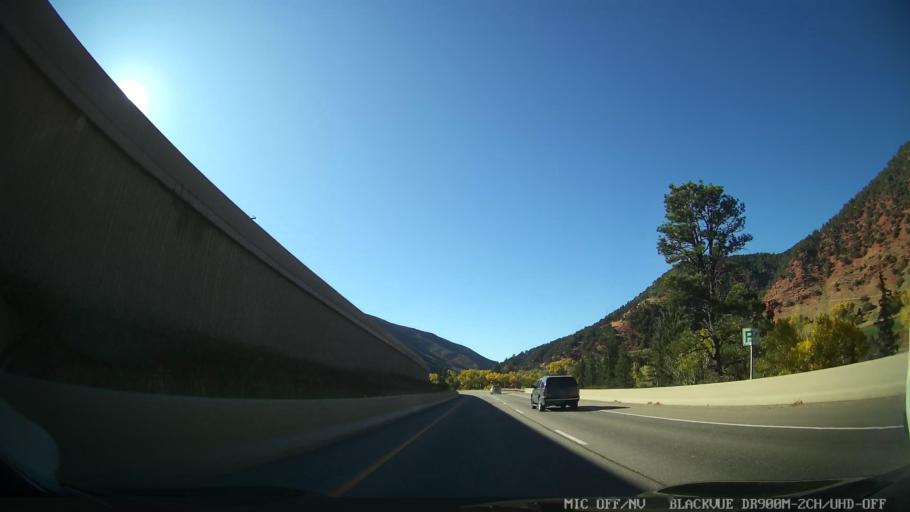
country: US
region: Colorado
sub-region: Eagle County
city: Basalt
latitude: 39.3300
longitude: -106.9767
